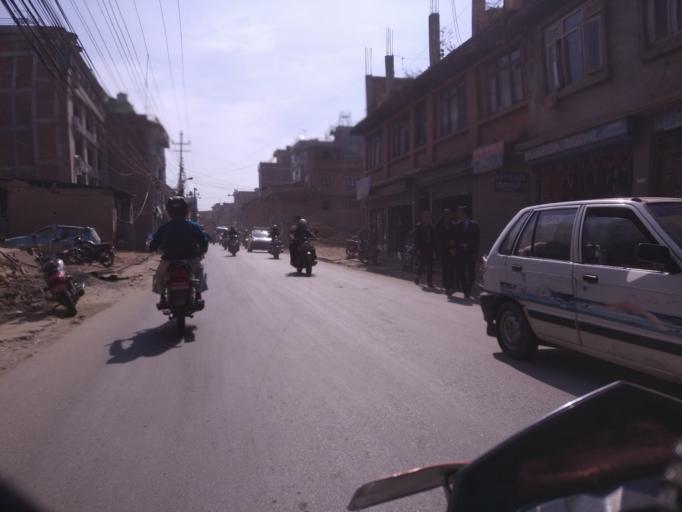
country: NP
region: Central Region
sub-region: Bagmati Zone
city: Patan
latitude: 27.6608
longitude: 85.3239
